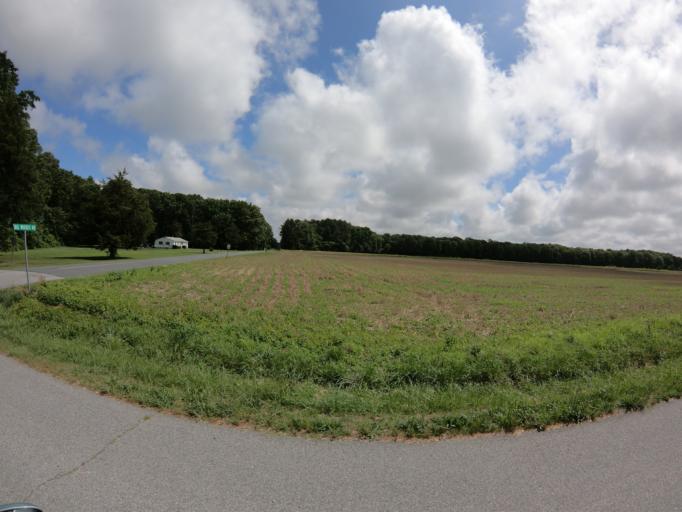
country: US
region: Maryland
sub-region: Caroline County
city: Ridgely
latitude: 39.1068
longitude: -75.8980
